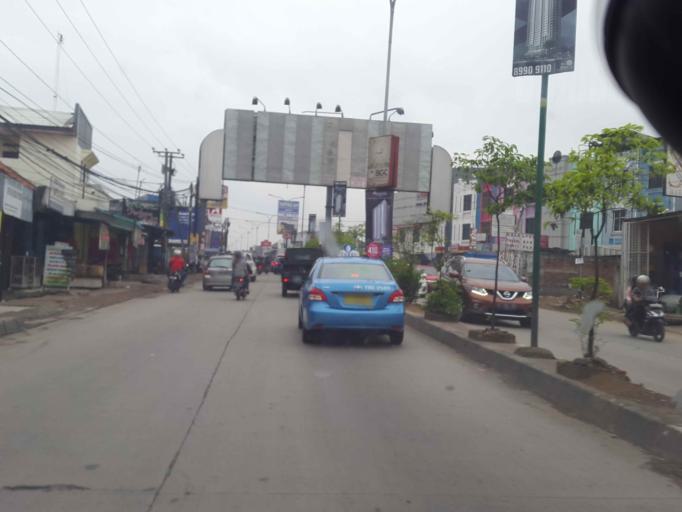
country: ID
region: West Java
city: Cikarang
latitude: -6.3185
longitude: 107.1354
